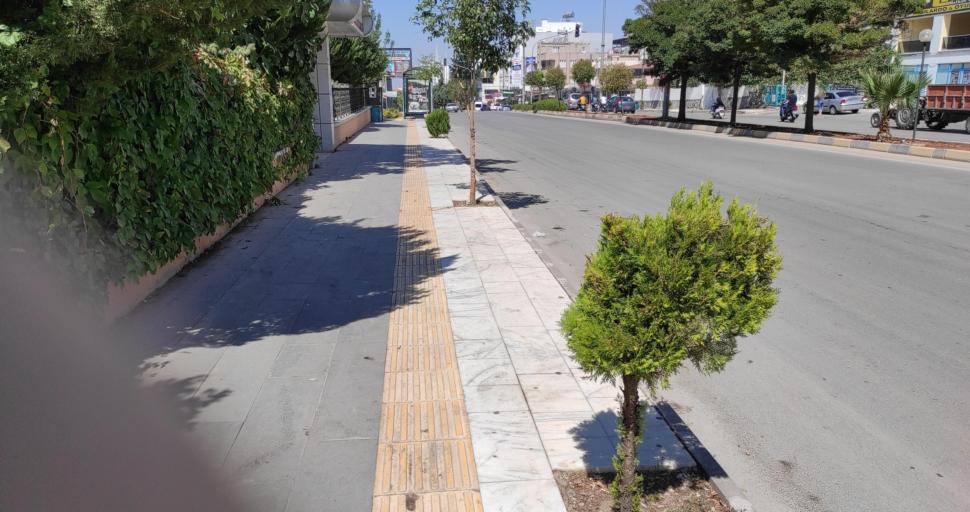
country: TR
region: Kilis
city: Kilis
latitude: 36.7265
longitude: 37.1019
